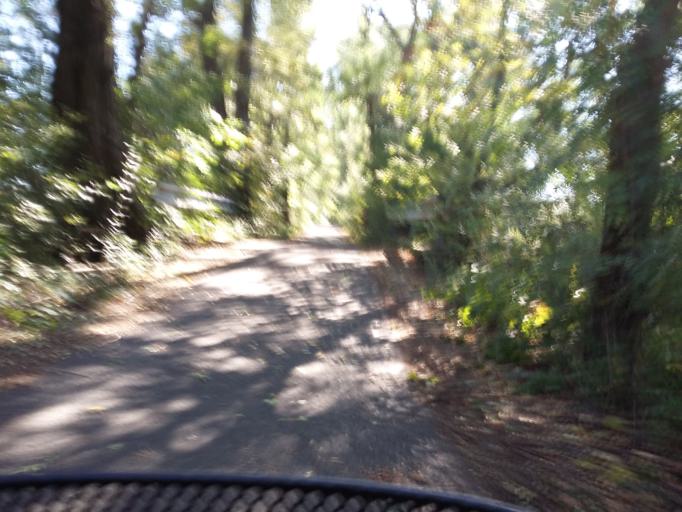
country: AT
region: Lower Austria
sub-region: Politischer Bezirk Ganserndorf
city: Marchegg
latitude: 48.2846
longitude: 16.9163
